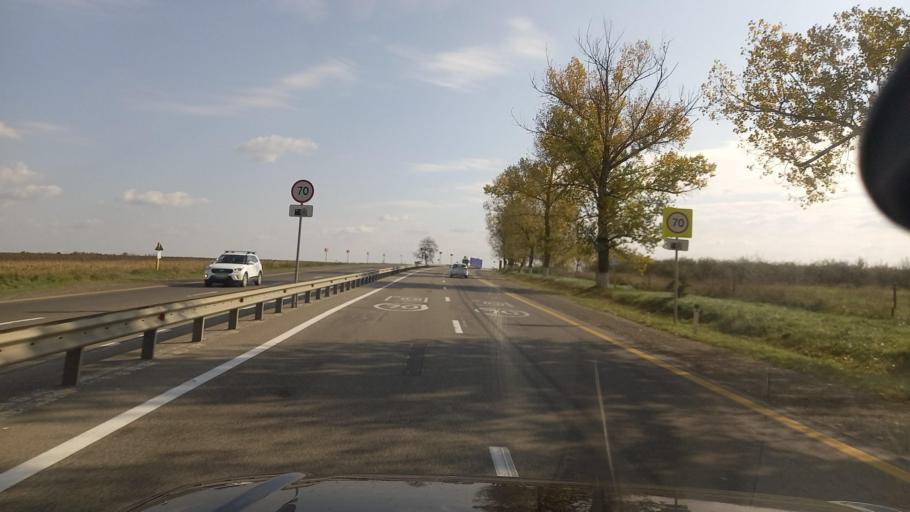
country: RU
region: Krasnodarskiy
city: Akhtyrskiy
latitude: 44.8543
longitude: 38.2610
